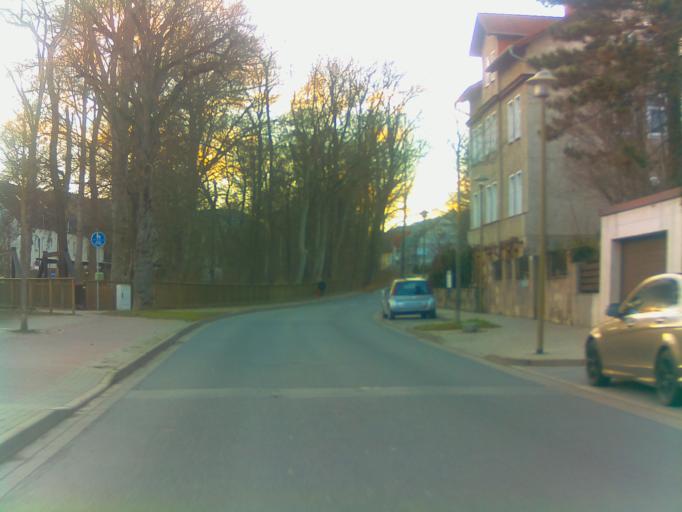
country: DE
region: Thuringia
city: Rudolstadt
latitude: 50.7166
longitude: 11.3186
